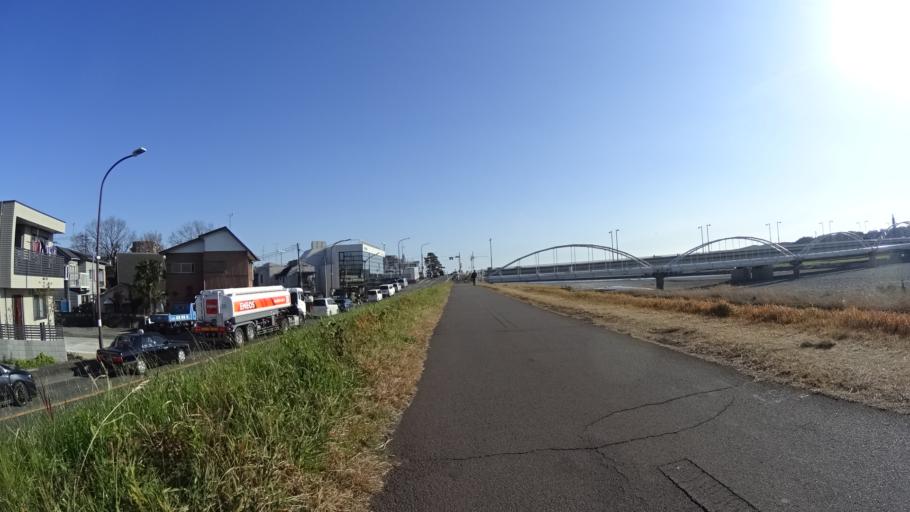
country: JP
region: Tokyo
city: Chofugaoka
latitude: 35.6460
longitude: 139.5256
